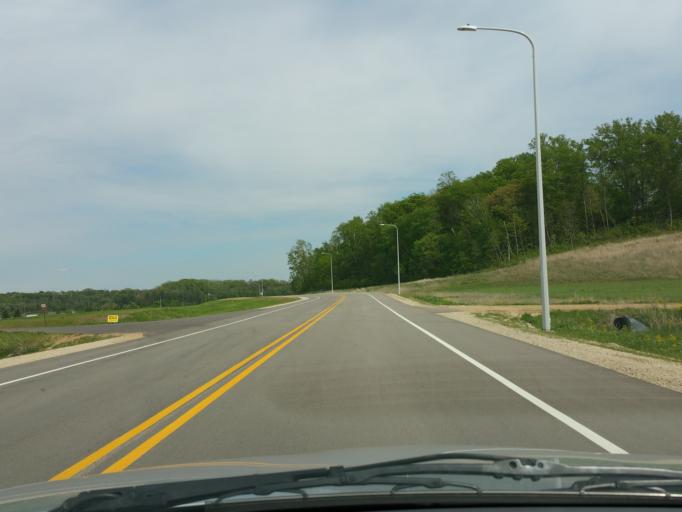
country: US
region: Wisconsin
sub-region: Pierce County
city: River Falls
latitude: 44.8944
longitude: -92.6452
